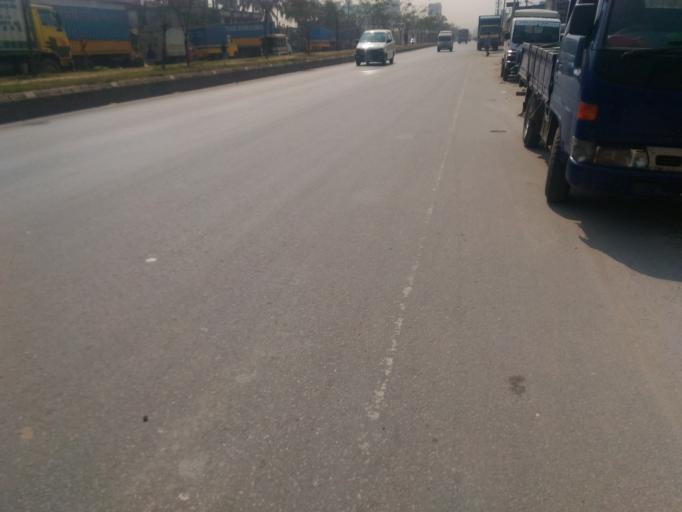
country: BD
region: Dhaka
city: Tungi
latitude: 24.0059
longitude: 90.3833
